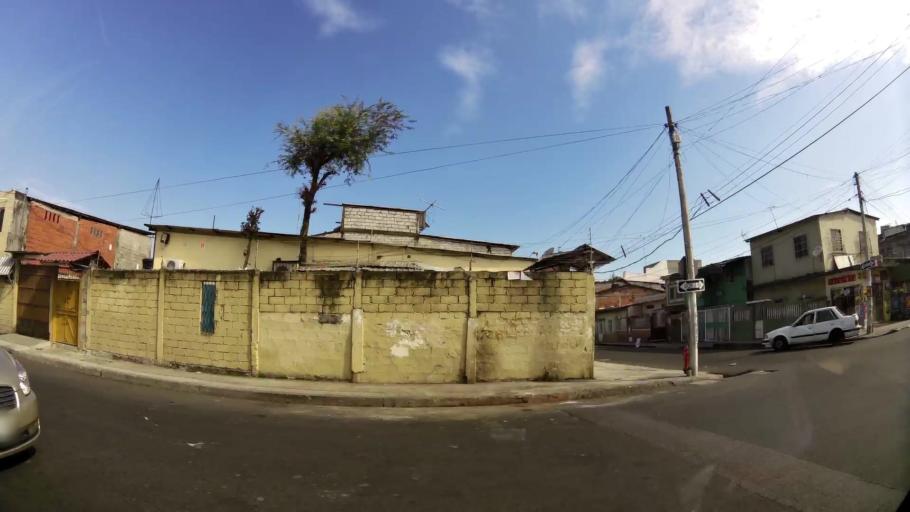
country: EC
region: Guayas
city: Guayaquil
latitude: -2.2135
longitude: -79.9132
